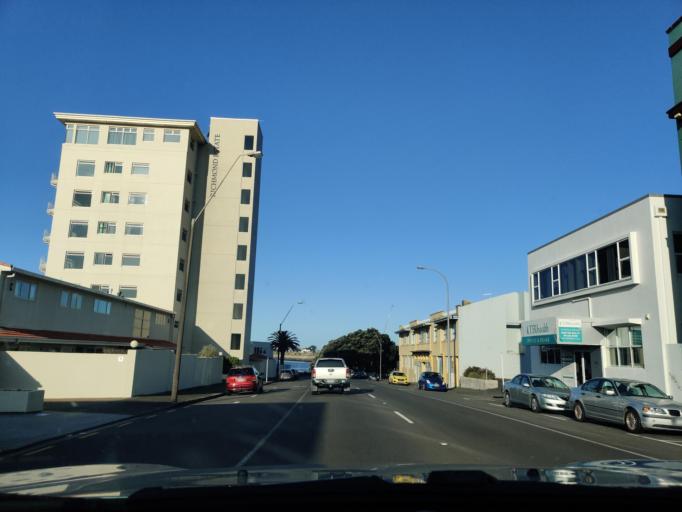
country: NZ
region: Taranaki
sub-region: New Plymouth District
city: New Plymouth
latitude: -39.0569
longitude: 174.0676
